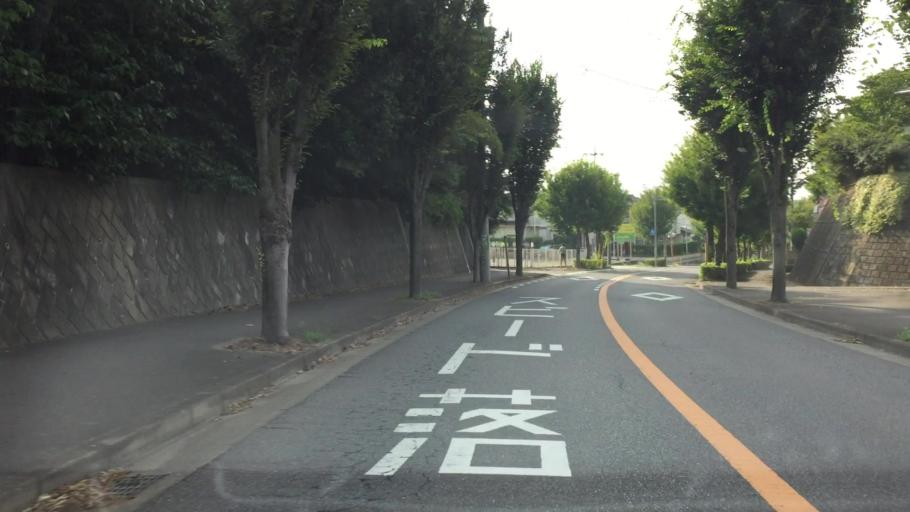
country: JP
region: Ibaraki
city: Toride
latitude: 35.8608
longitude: 140.1145
